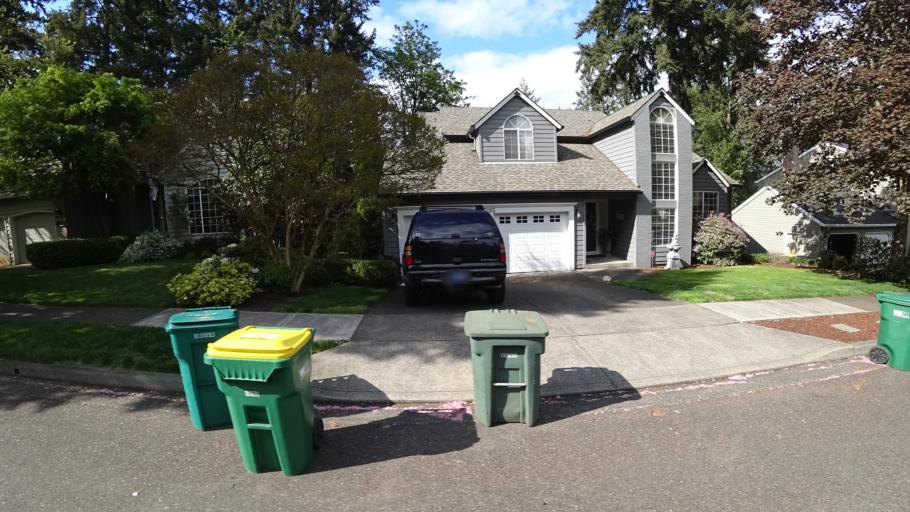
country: US
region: Oregon
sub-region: Washington County
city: Beaverton
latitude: 45.4460
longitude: -122.8319
